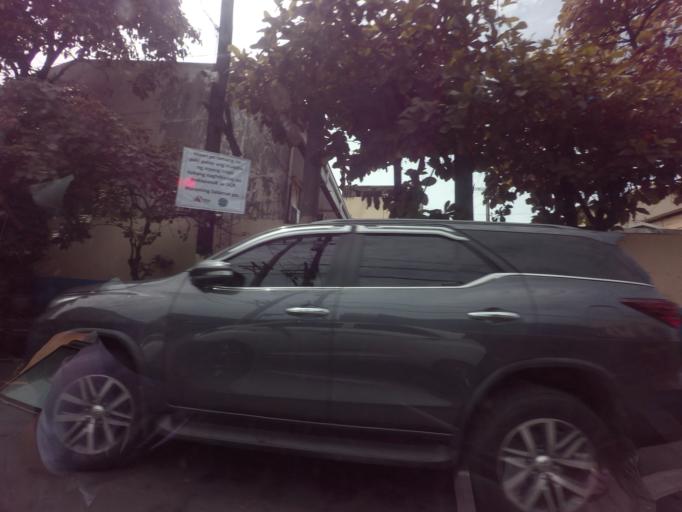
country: PH
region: Calabarzon
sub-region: Province of Rizal
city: Pateros
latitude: 14.5610
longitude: 121.0701
